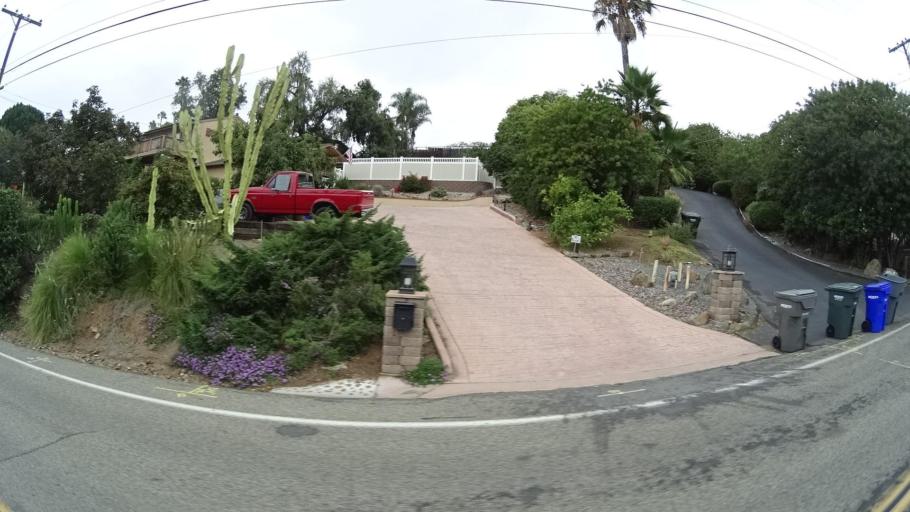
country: US
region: California
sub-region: San Diego County
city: Casa de Oro-Mount Helix
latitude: 32.7604
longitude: -116.9825
